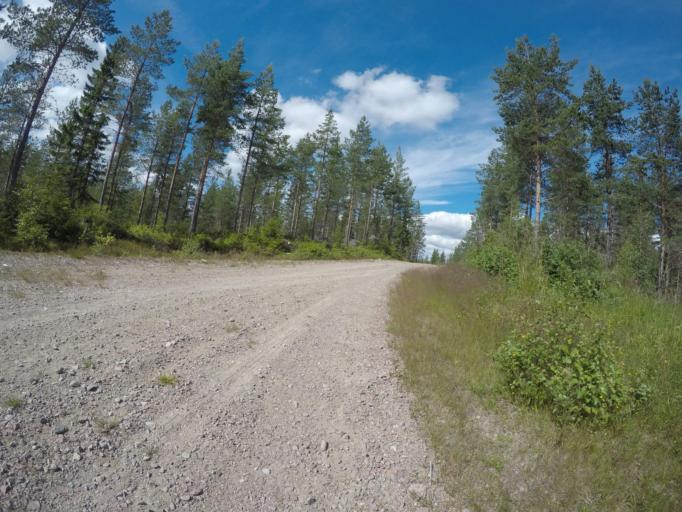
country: SE
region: OErebro
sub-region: Hallefors Kommun
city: Haellefors
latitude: 60.0853
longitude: 14.4911
